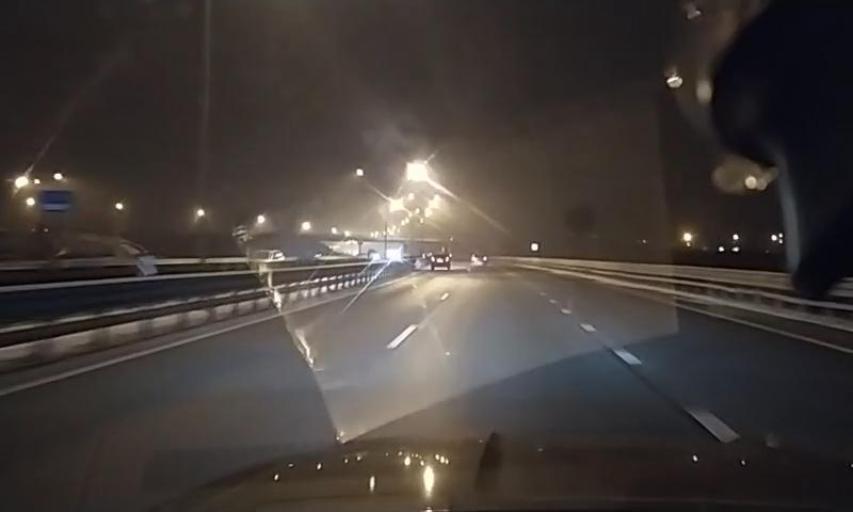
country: RU
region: Leningrad
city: Bugry
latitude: 60.0988
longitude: 30.3826
